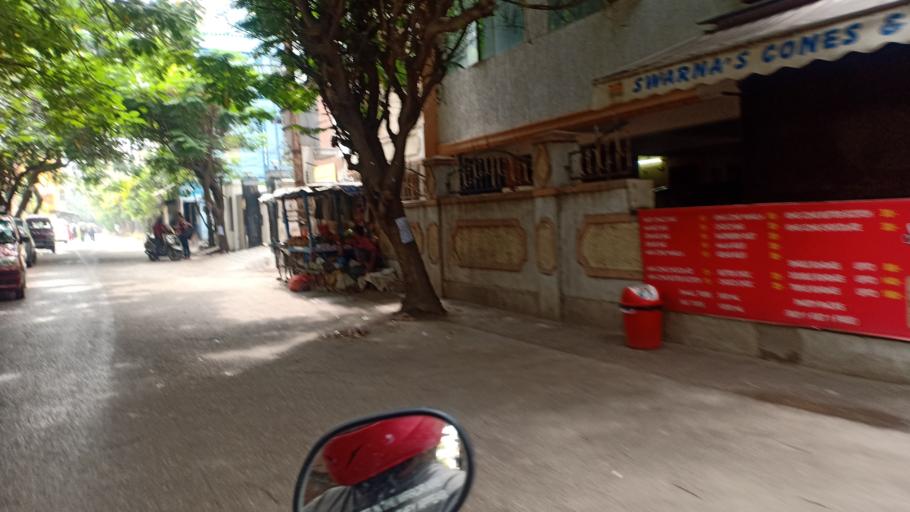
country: IN
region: Telangana
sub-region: Hyderabad
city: Hyderabad
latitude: 17.4361
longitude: 78.4411
